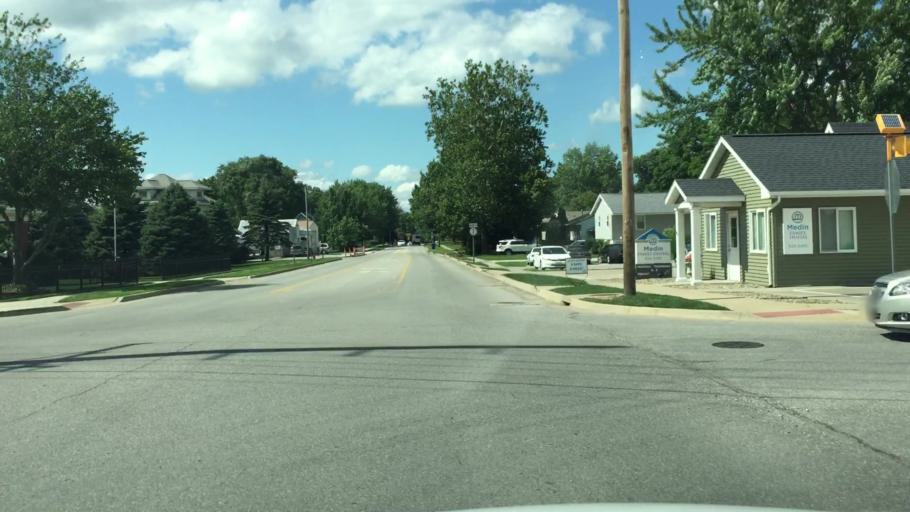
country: US
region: Iowa
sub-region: Johnson County
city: Solon
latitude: 41.8021
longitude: -91.4916
